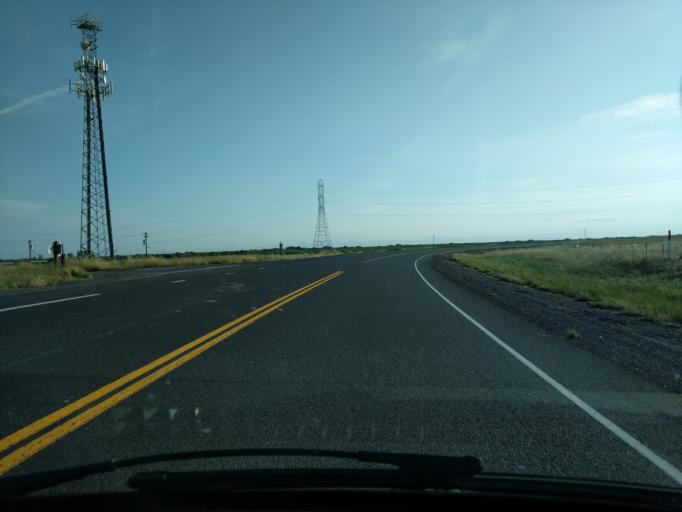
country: US
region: California
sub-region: San Joaquin County
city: Escalon
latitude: 37.9315
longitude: -120.9462
